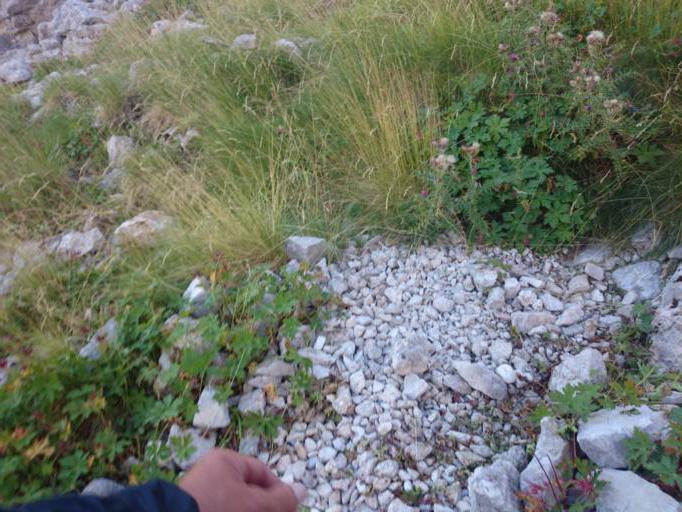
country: AL
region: Elbasan
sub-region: Rrethi i Gramshit
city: Kushove
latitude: 40.7226
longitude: 20.1438
